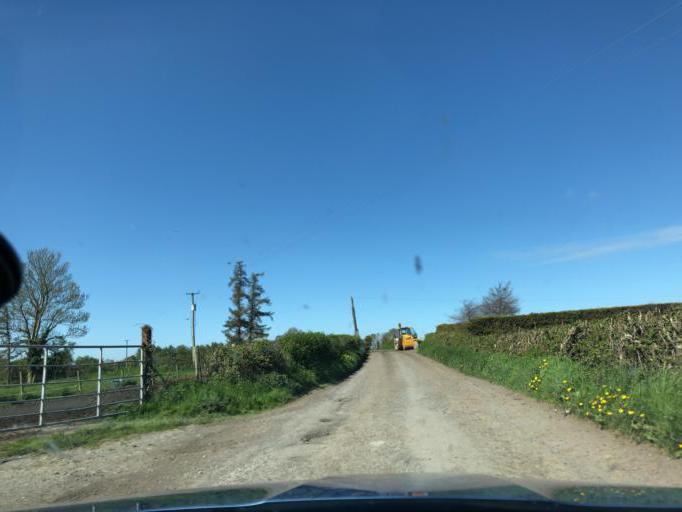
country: IE
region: Connaught
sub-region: County Galway
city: Portumna
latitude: 53.1789
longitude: -8.1884
